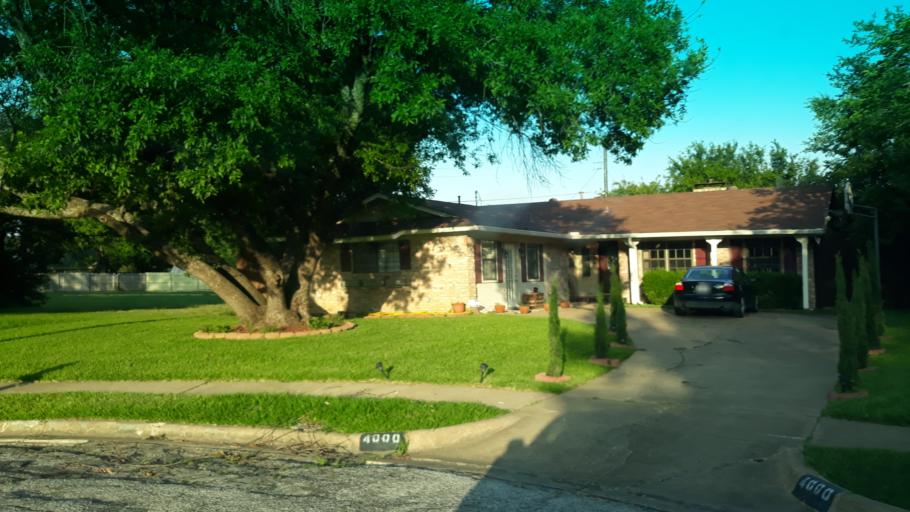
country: US
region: Texas
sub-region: Dallas County
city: Irving
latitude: 32.8529
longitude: -97.0045
